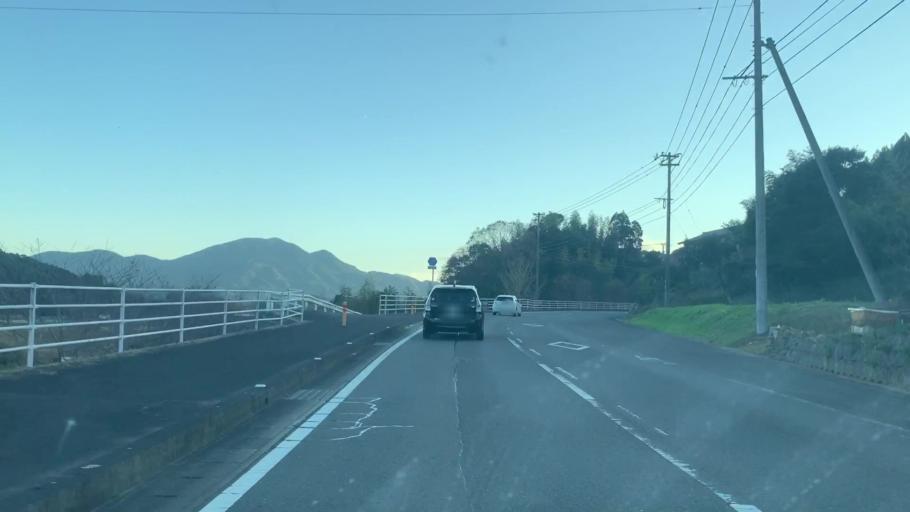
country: JP
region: Saga Prefecture
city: Imaricho-ko
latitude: 33.3229
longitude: 129.9698
